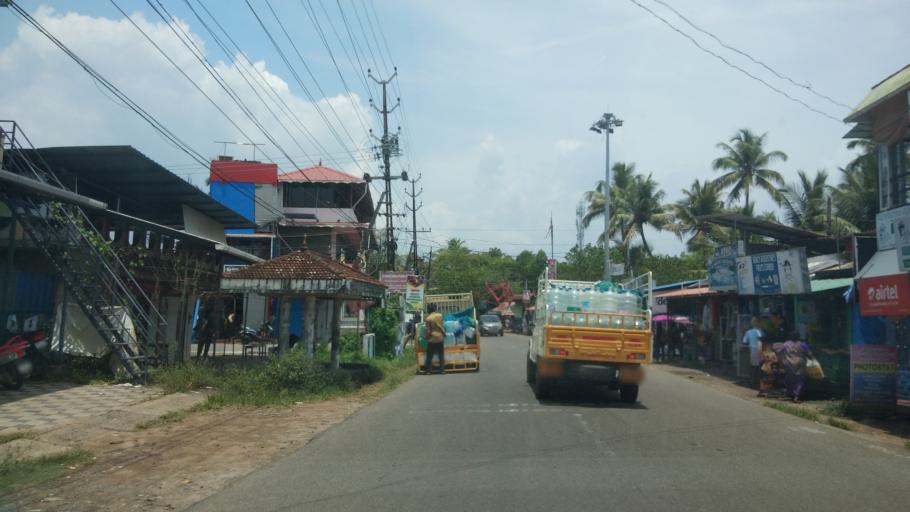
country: IN
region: Kerala
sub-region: Alappuzha
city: Arukutti
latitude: 9.8555
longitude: 76.2672
